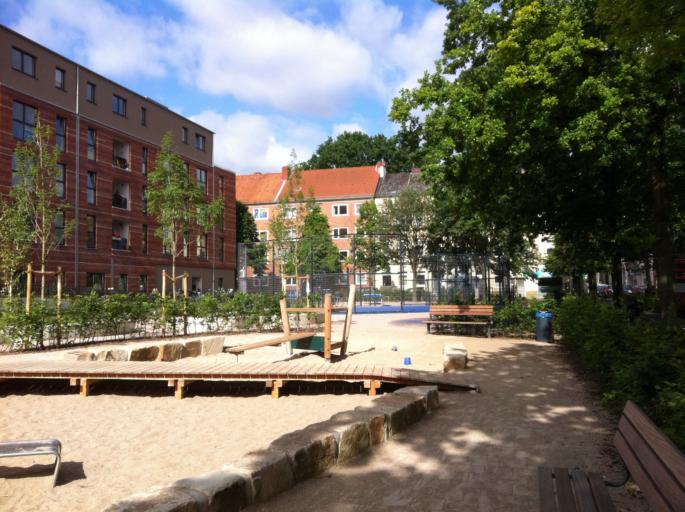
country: DE
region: Hamburg
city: Altona
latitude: 53.5523
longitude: 9.9471
